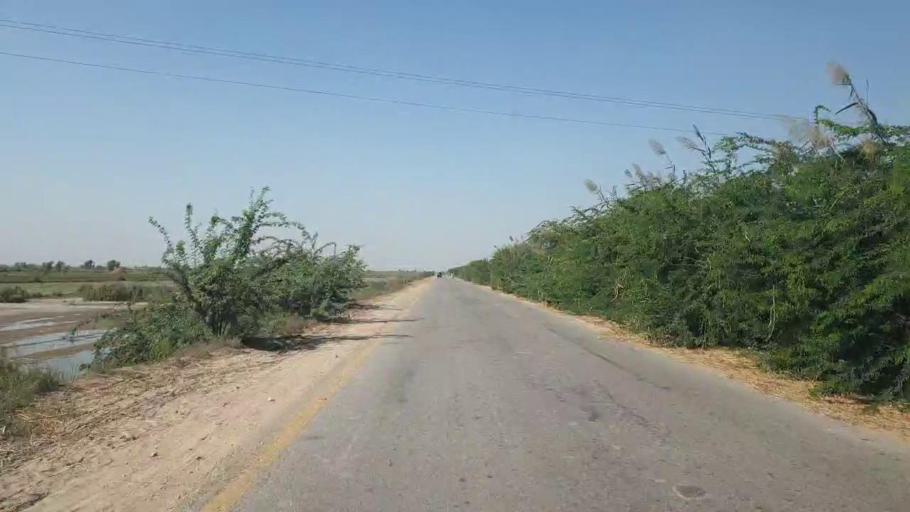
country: PK
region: Sindh
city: Rajo Khanani
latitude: 25.0490
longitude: 68.8092
